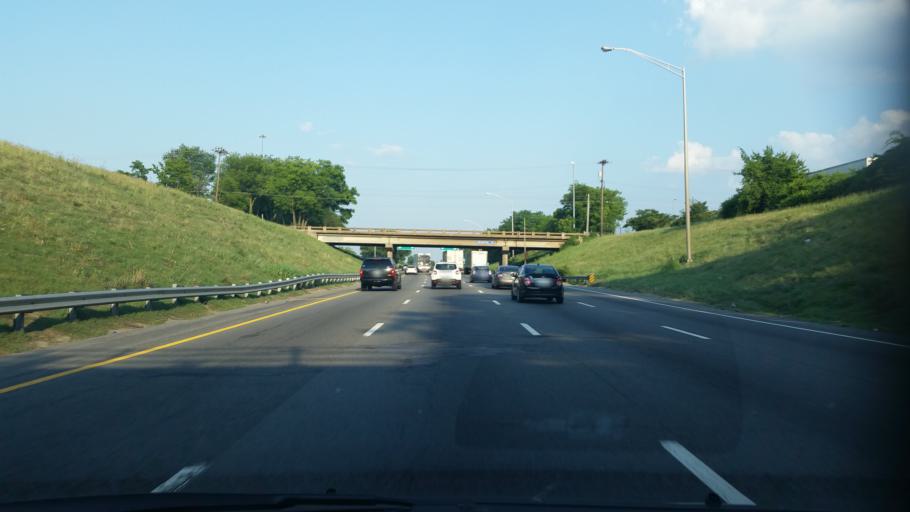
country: US
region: Tennessee
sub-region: Davidson County
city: Nashville
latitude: 36.1412
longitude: -86.7335
